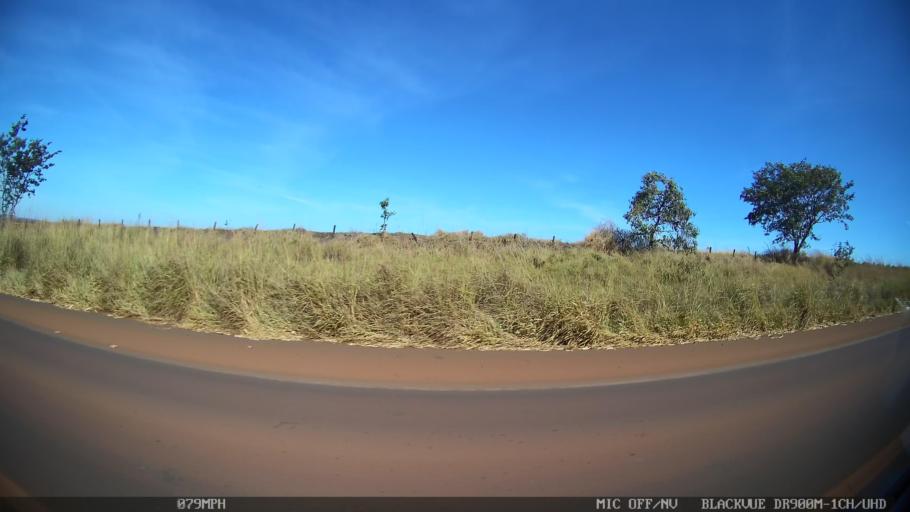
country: BR
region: Sao Paulo
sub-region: Sao Joaquim Da Barra
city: Sao Joaquim da Barra
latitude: -20.5597
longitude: -47.6964
